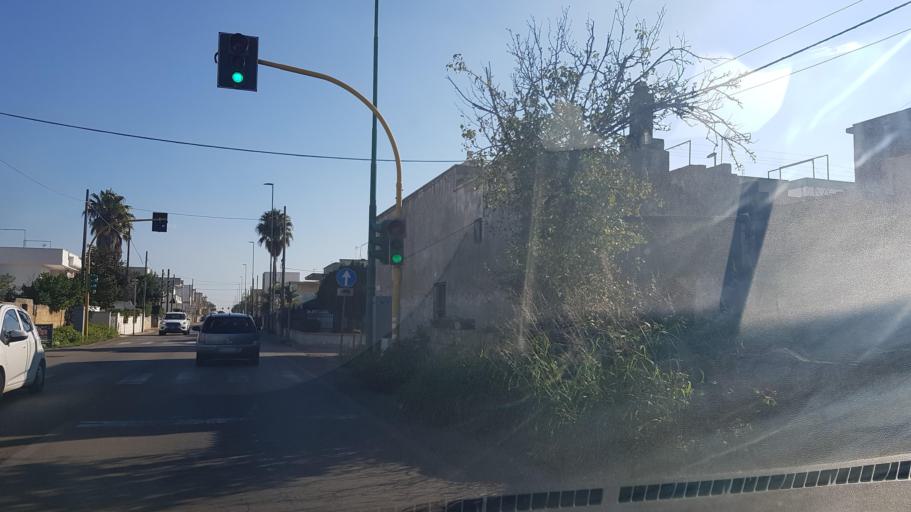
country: IT
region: Apulia
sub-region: Provincia di Lecce
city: Montesano Salentino
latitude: 39.9805
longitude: 18.3238
